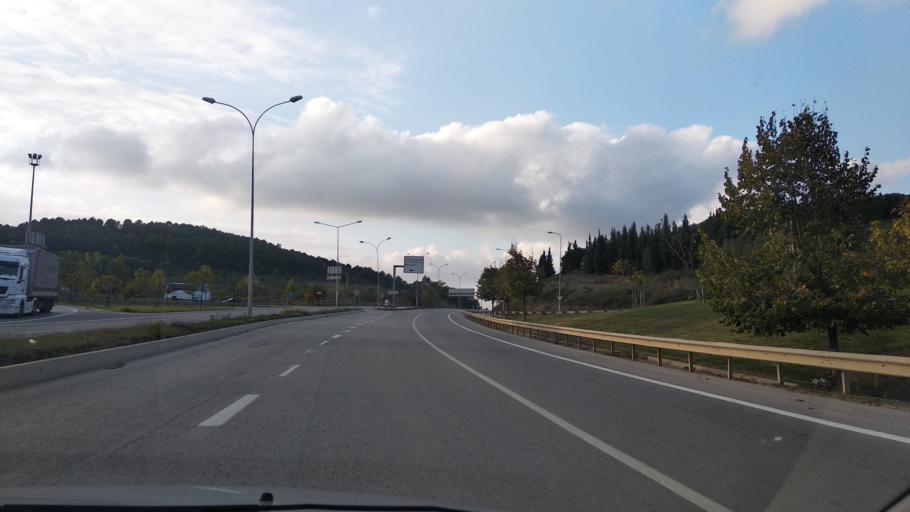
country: TR
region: Istanbul
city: Sultanbeyli
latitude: 40.9227
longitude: 29.3405
